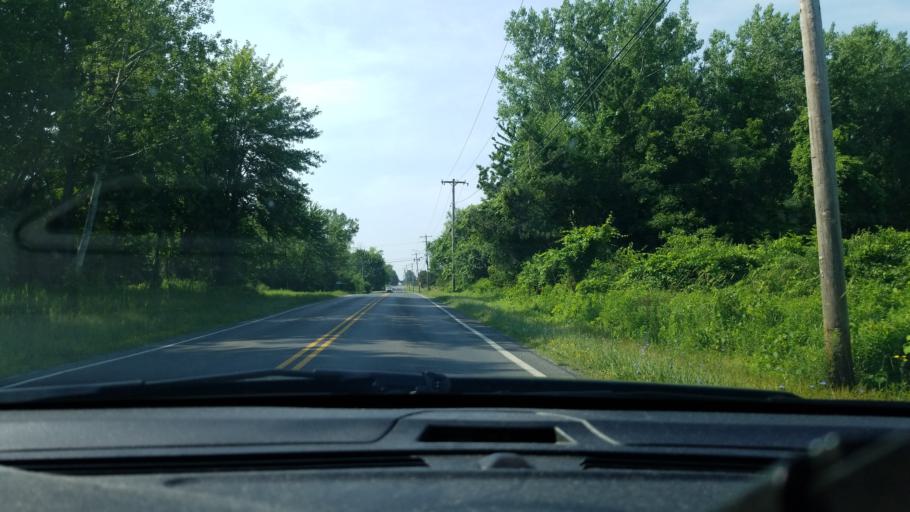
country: US
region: New York
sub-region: Onondaga County
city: East Syracuse
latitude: 43.1112
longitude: -76.0731
